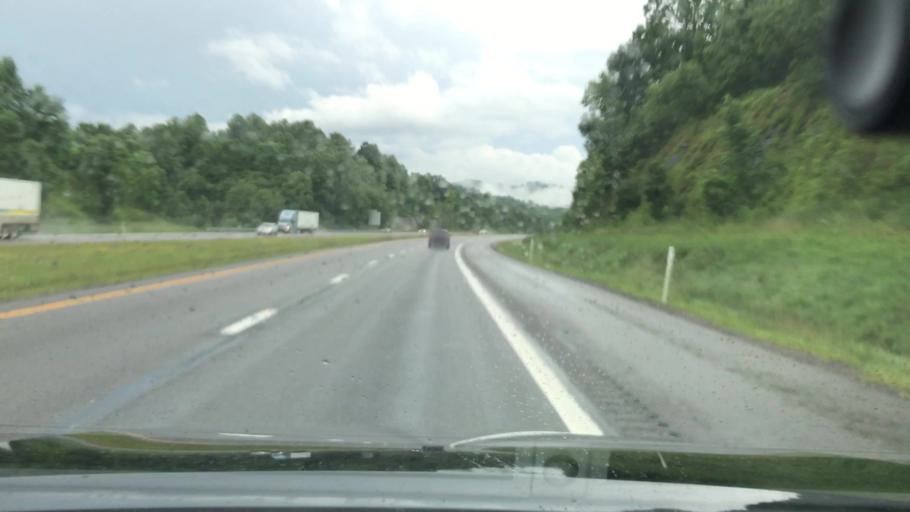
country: US
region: West Virginia
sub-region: Raleigh County
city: Bradley
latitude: 37.9521
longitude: -81.2565
